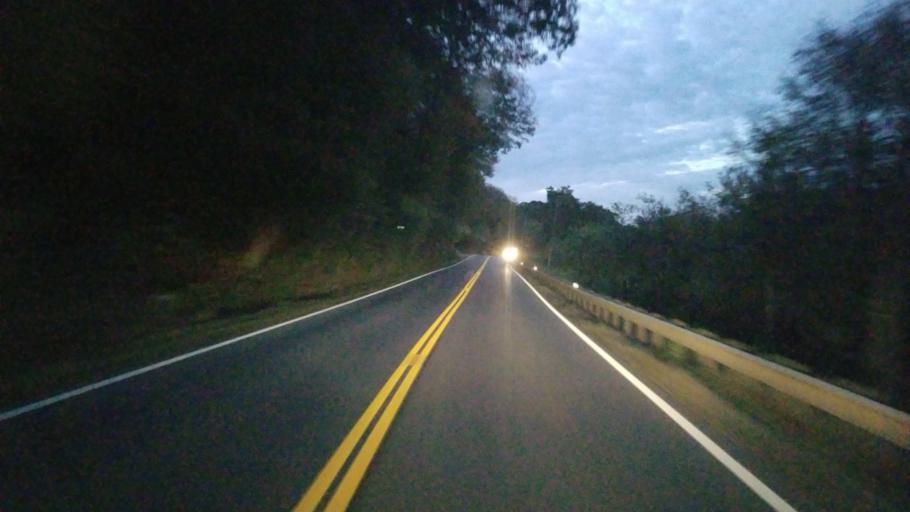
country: US
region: Ohio
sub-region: Scioto County
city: Rosemount
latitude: 38.8242
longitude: -83.0178
